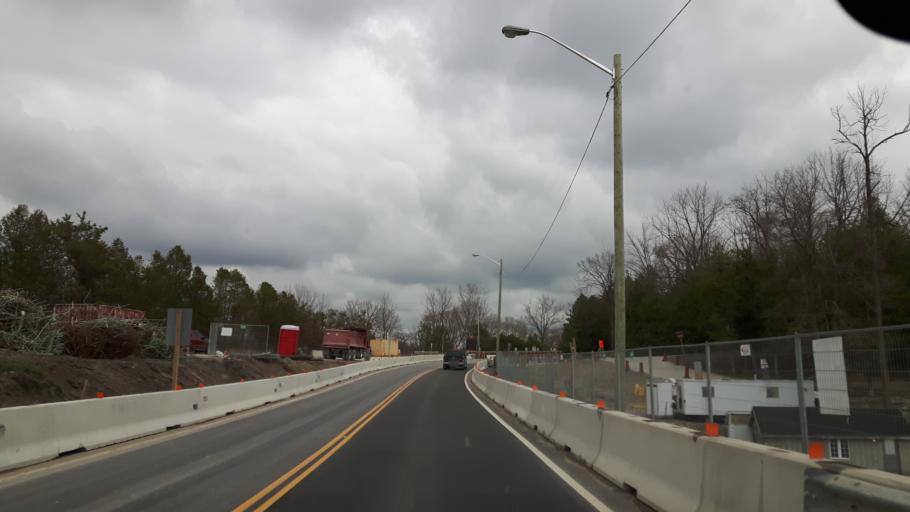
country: CA
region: Ontario
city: Bluewater
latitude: 43.5684
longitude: -81.6981
